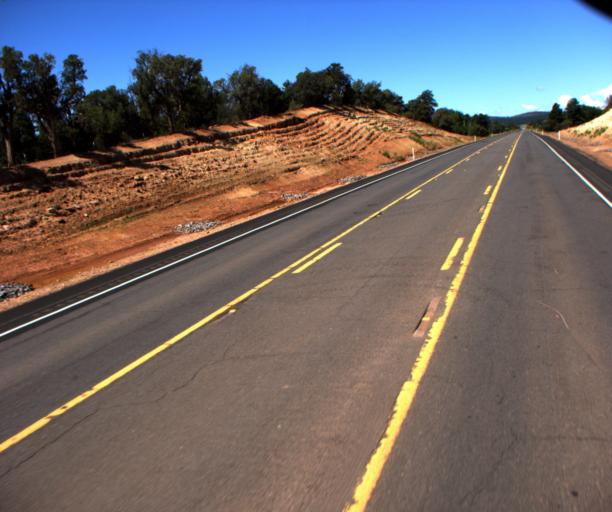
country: US
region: Arizona
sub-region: Navajo County
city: Linden
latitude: 34.2854
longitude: -110.1245
